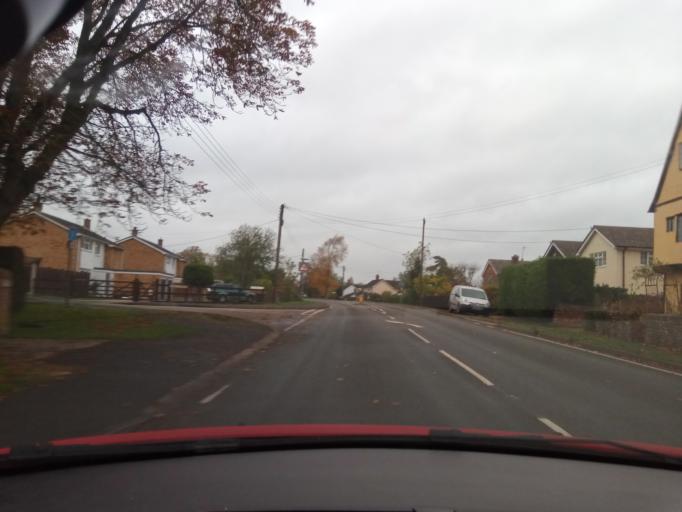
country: GB
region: England
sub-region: Essex
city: Great Yeldham
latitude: 52.0402
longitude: 0.5317
